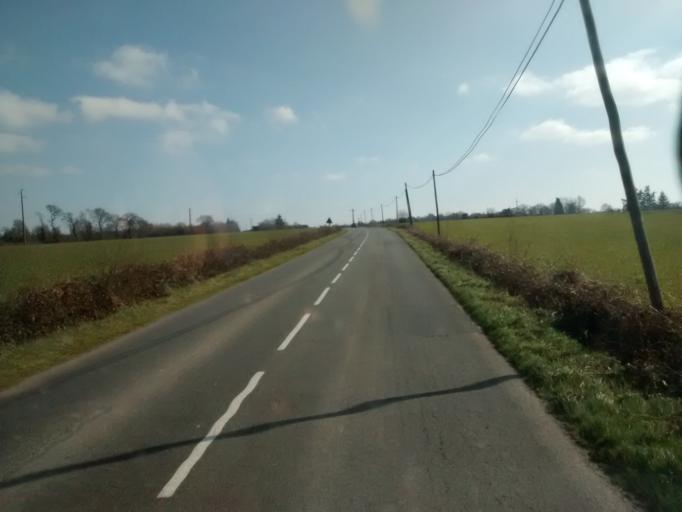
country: FR
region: Brittany
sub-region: Departement d'Ille-et-Vilaine
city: Paimpont
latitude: 48.0430
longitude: -2.1839
